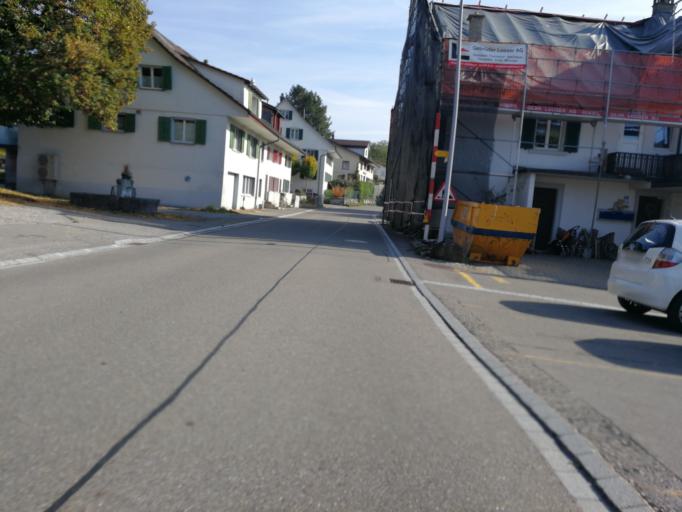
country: CH
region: Zurich
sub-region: Bezirk Hinwil
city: Hadlikon
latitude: 47.2811
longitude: 8.8607
